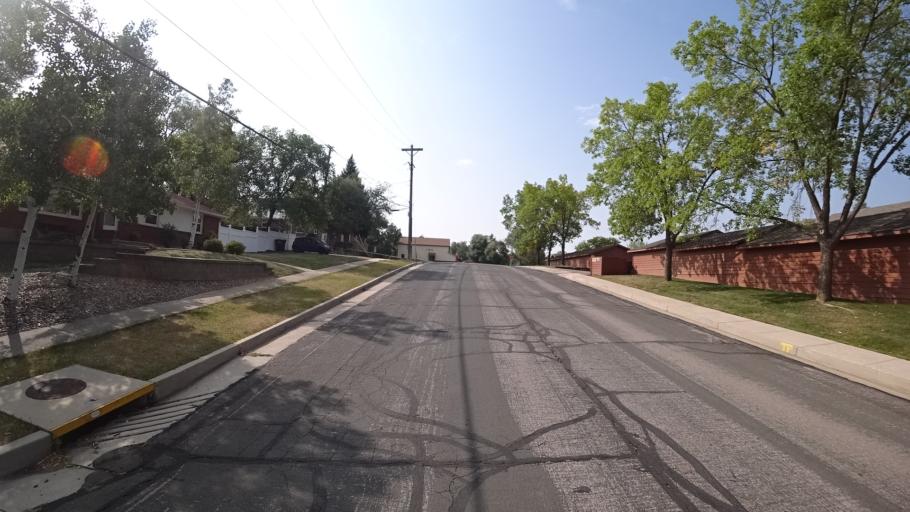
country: US
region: Colorado
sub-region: El Paso County
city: Colorado Springs
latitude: 38.8550
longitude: -104.7848
